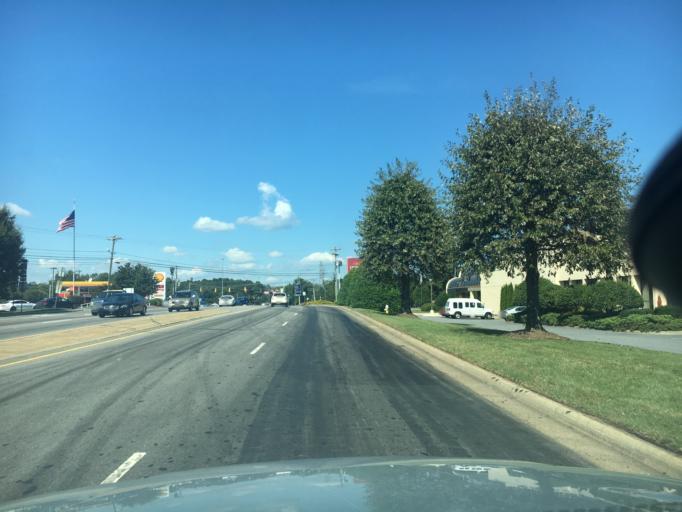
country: US
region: North Carolina
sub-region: Catawba County
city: Hickory
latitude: 35.7094
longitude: -81.3113
